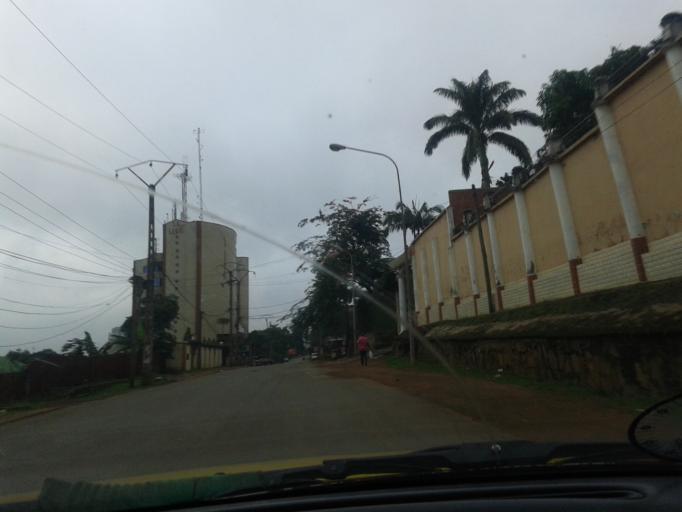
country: CM
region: Centre
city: Yaounde
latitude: 3.8758
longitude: 11.5181
